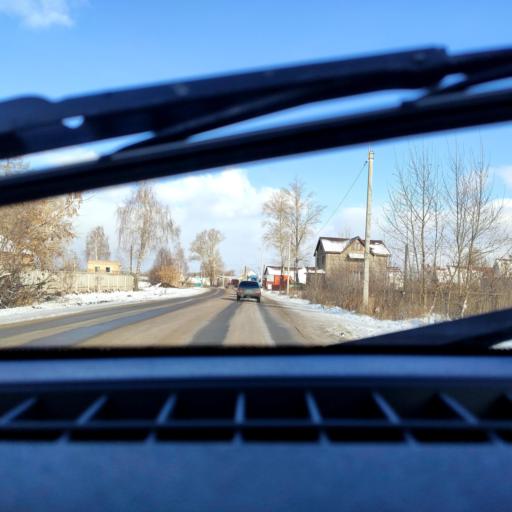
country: RU
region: Bashkortostan
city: Iglino
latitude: 54.8193
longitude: 56.3959
